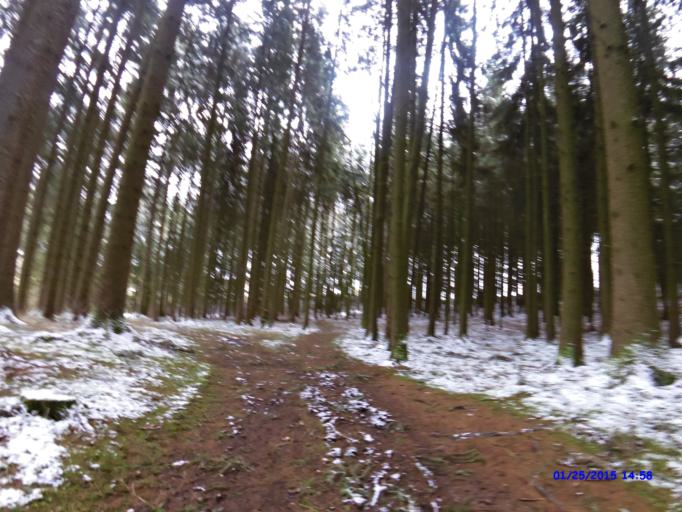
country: DE
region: Bavaria
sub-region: Lower Bavaria
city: Eching
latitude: 48.4985
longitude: 12.0817
